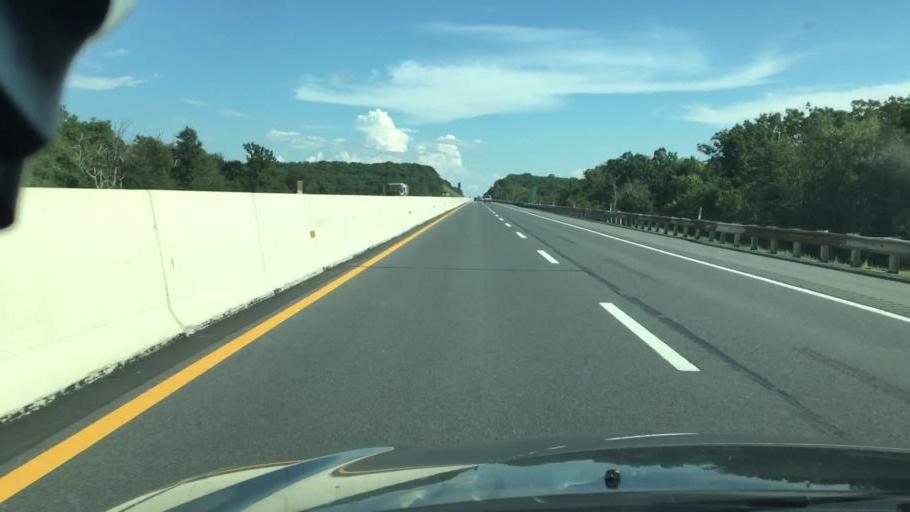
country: US
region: Pennsylvania
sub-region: Carbon County
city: Towamensing Trails
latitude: 41.0471
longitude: -75.6714
